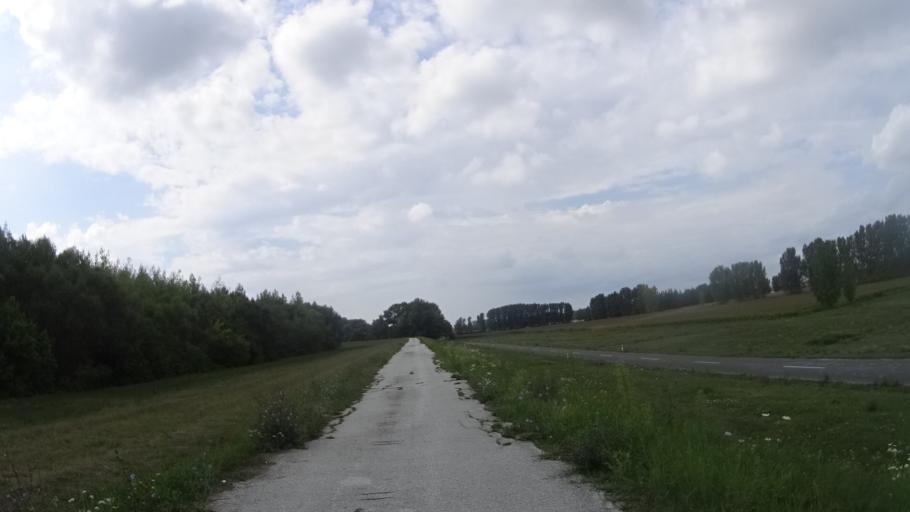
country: SK
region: Trnavsky
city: Gabcikovo
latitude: 47.8065
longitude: 17.6422
